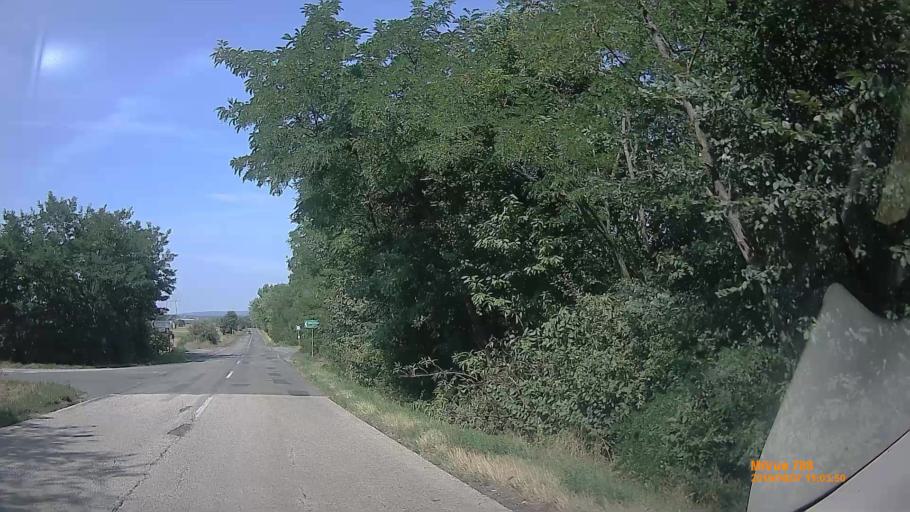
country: HU
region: Veszprem
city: Ajka
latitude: 47.0223
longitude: 17.5043
